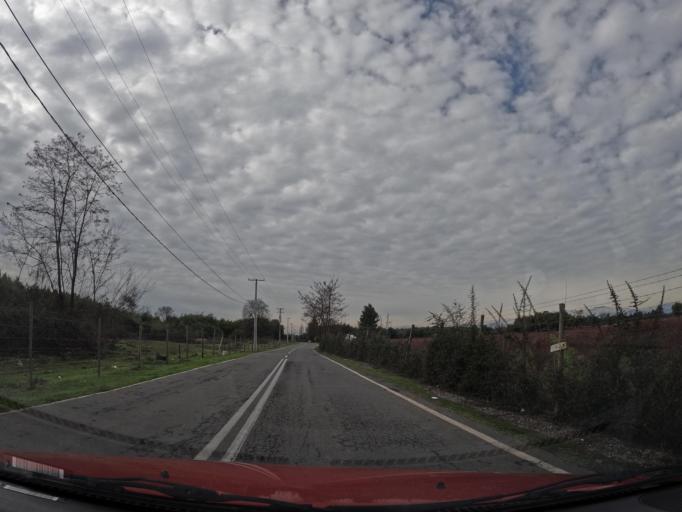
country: CL
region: Maule
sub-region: Provincia de Linares
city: Linares
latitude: -35.8657
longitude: -71.6229
